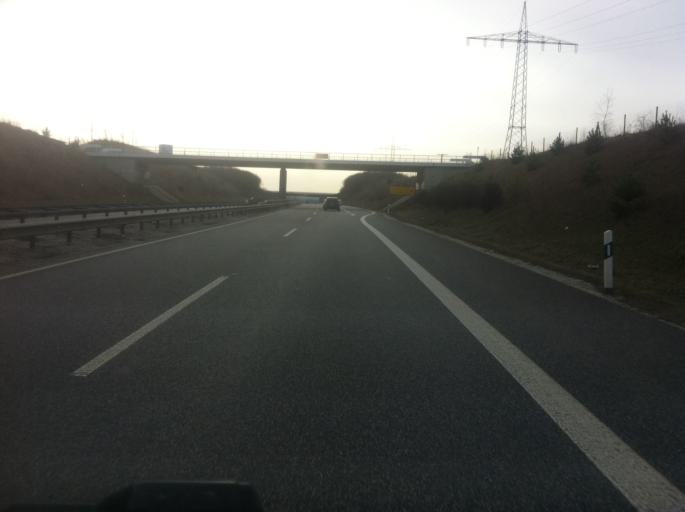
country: DE
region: Rheinland-Pfalz
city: Kirchberg
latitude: 49.9553
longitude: 7.4072
